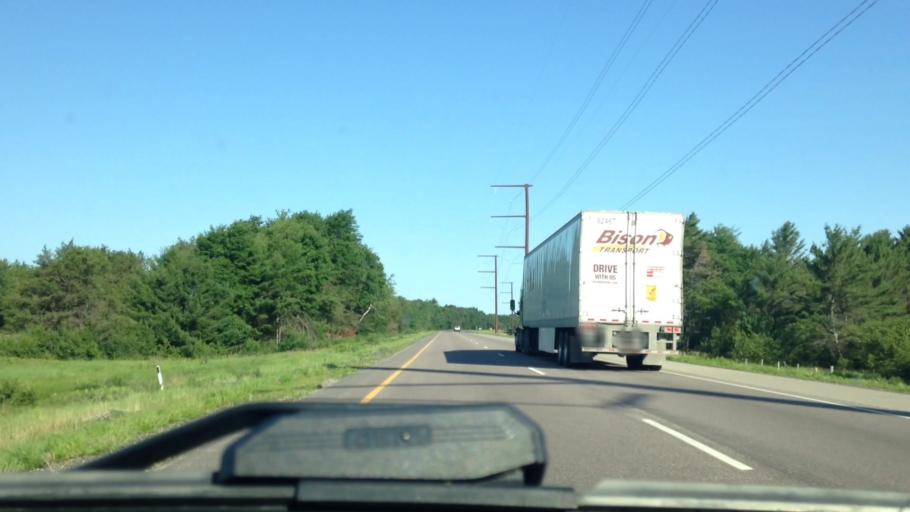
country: US
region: Wisconsin
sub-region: Monroe County
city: Tomah
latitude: 44.1702
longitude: -90.5912
